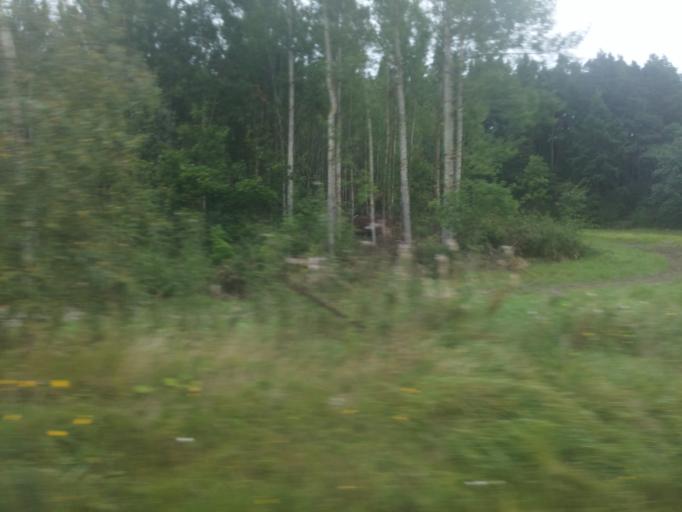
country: SE
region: OEstergoetland
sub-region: Norrkopings Kommun
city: Krokek
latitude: 58.5791
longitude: 16.3663
